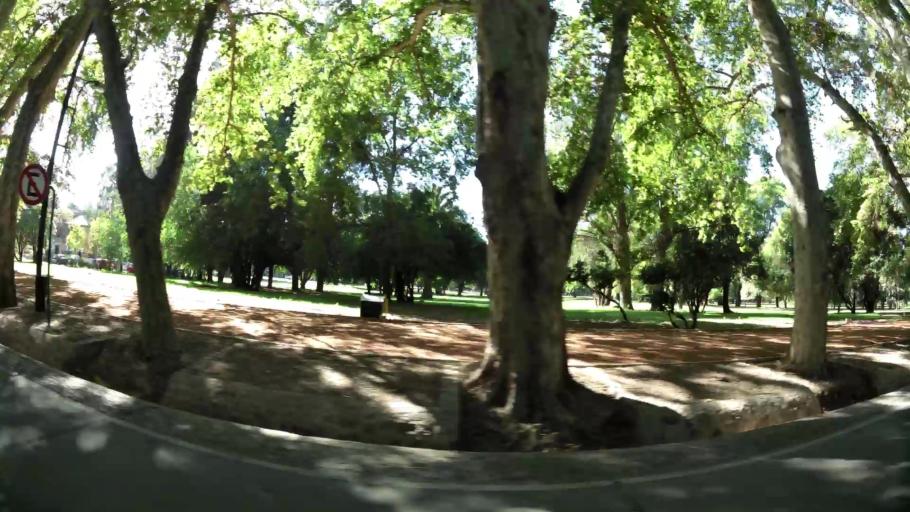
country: AR
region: Mendoza
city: Mendoza
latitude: -32.8878
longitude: -68.8633
